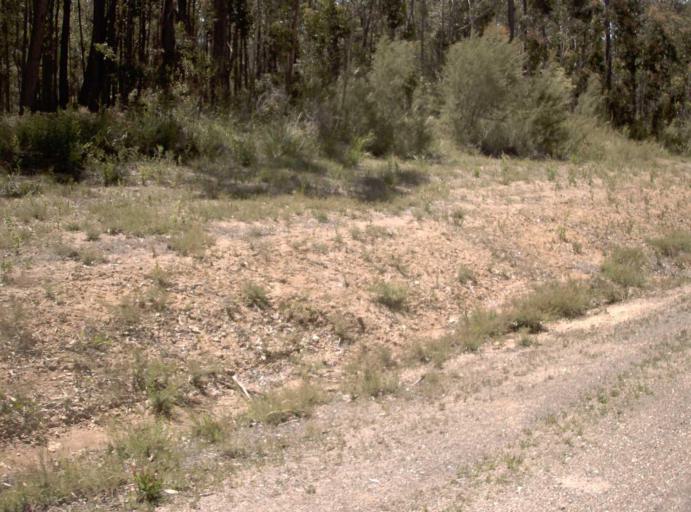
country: AU
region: Victoria
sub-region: East Gippsland
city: Lakes Entrance
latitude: -37.6819
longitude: 148.7713
